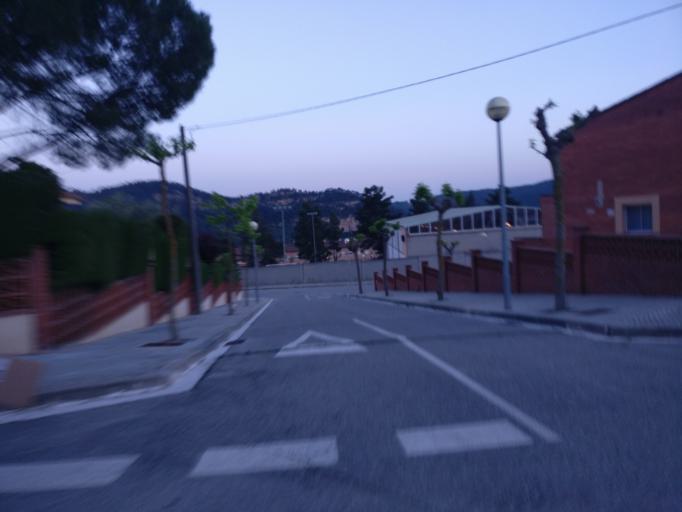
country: ES
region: Catalonia
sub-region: Provincia de Barcelona
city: Capellades
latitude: 41.5172
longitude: 1.7062
